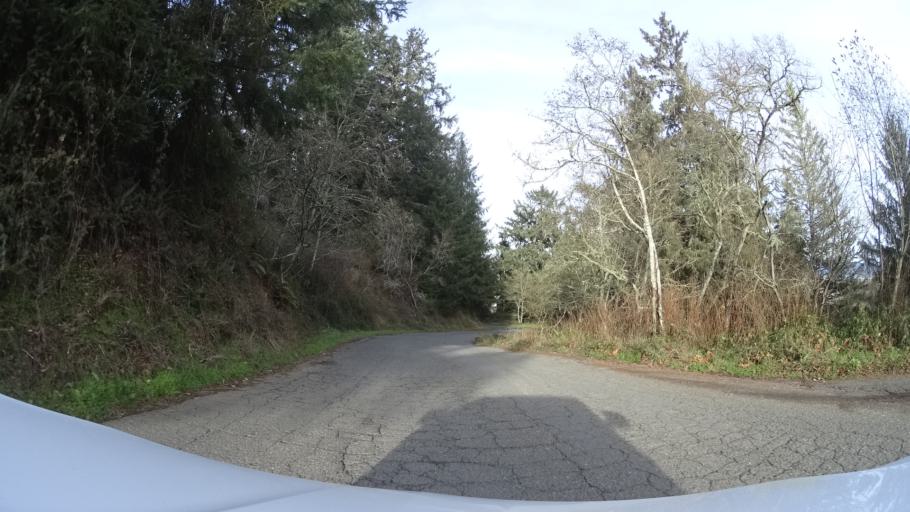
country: US
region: California
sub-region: Humboldt County
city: Ferndale
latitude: 40.5740
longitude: -124.2681
